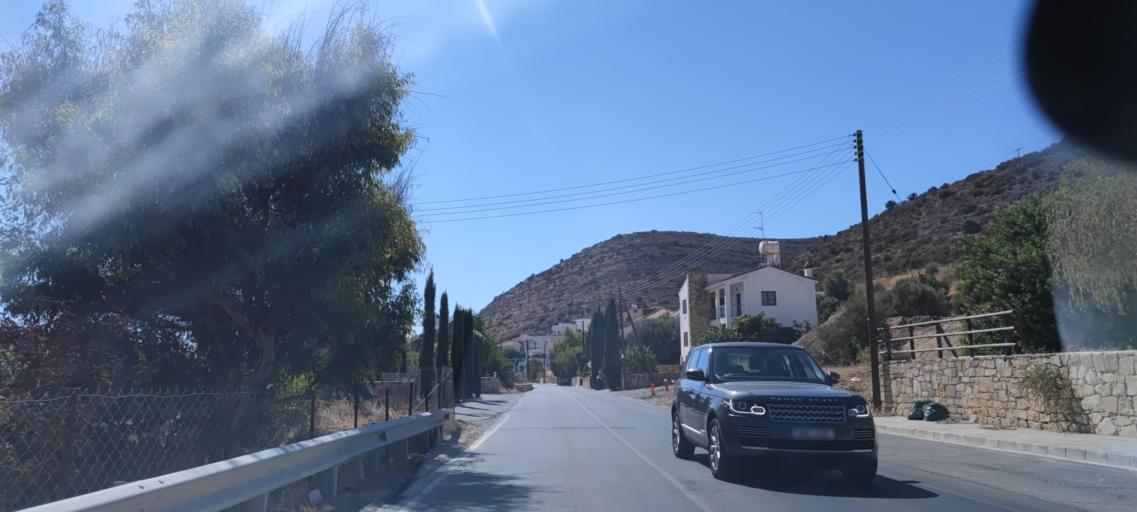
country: CY
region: Limassol
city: Mouttagiaka
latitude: 34.7361
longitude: 33.0830
